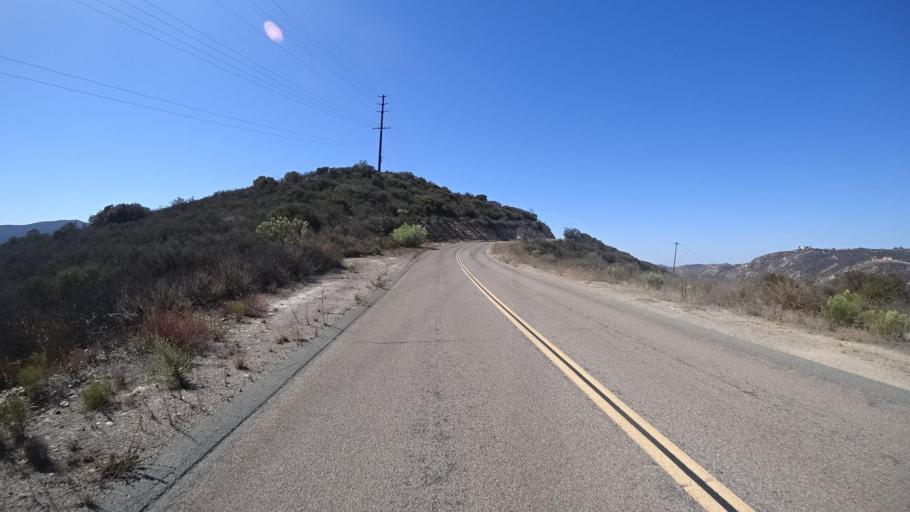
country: US
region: California
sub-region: San Diego County
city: Alpine
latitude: 32.7980
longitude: -116.7781
